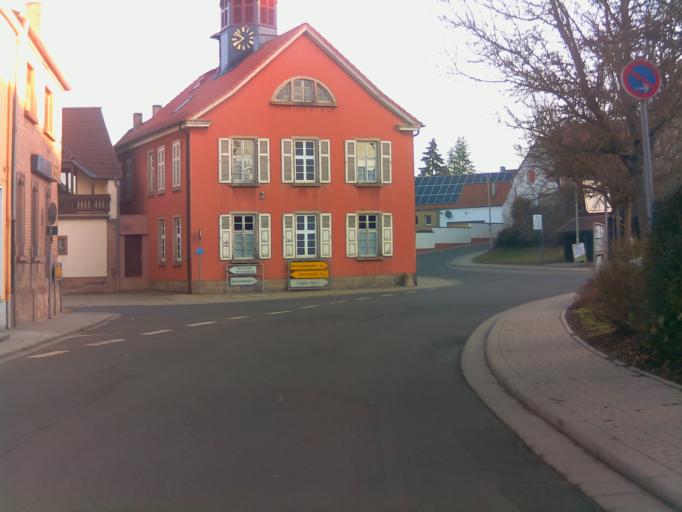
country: DE
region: Rheinland-Pfalz
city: Bolanden
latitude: 49.6389
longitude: 8.0115
